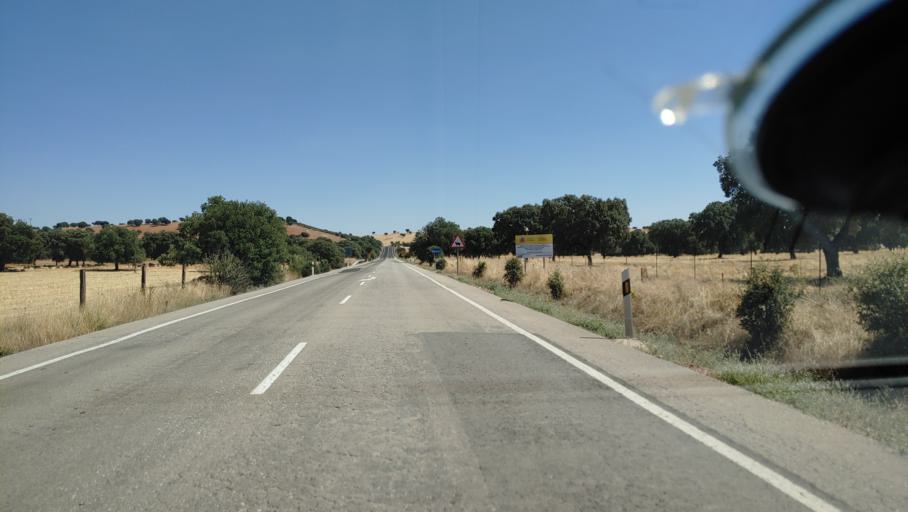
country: ES
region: Castille-La Mancha
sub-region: Provincia de Ciudad Real
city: Saceruela
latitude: 39.0165
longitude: -4.4740
